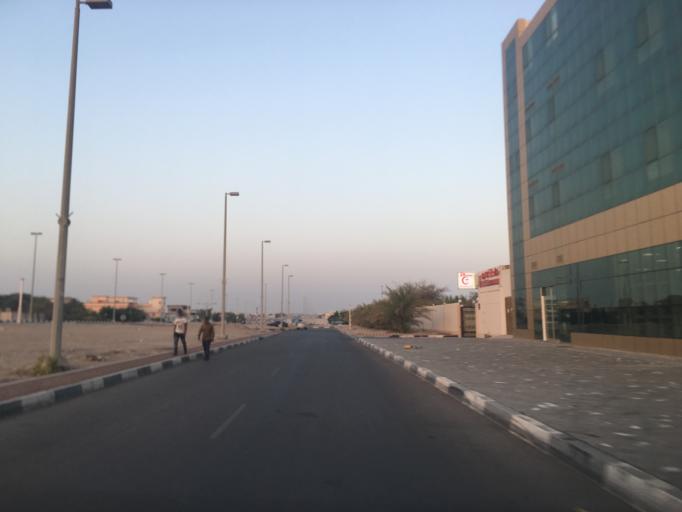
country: AE
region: Abu Dhabi
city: Abu Dhabi
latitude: 24.3055
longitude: 54.6377
